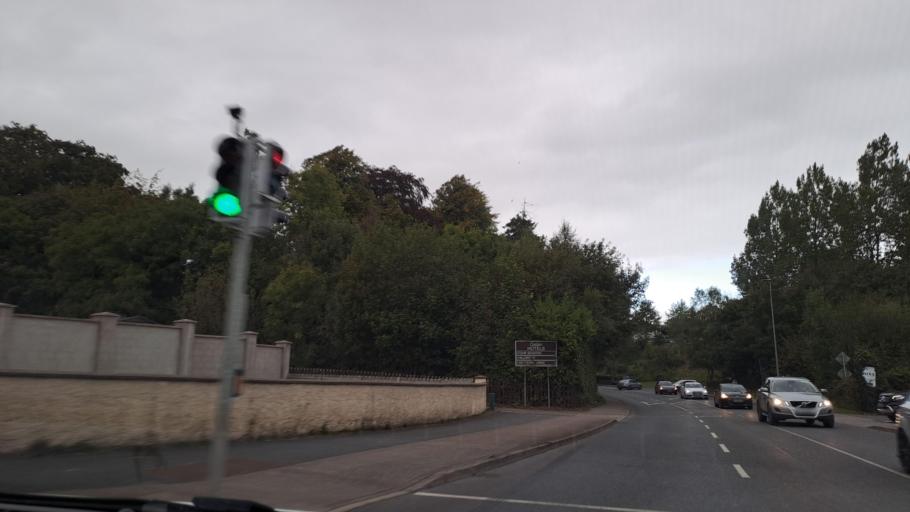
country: IE
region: Ulster
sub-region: County Monaghan
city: Monaghan
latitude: 54.2389
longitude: -6.9684
